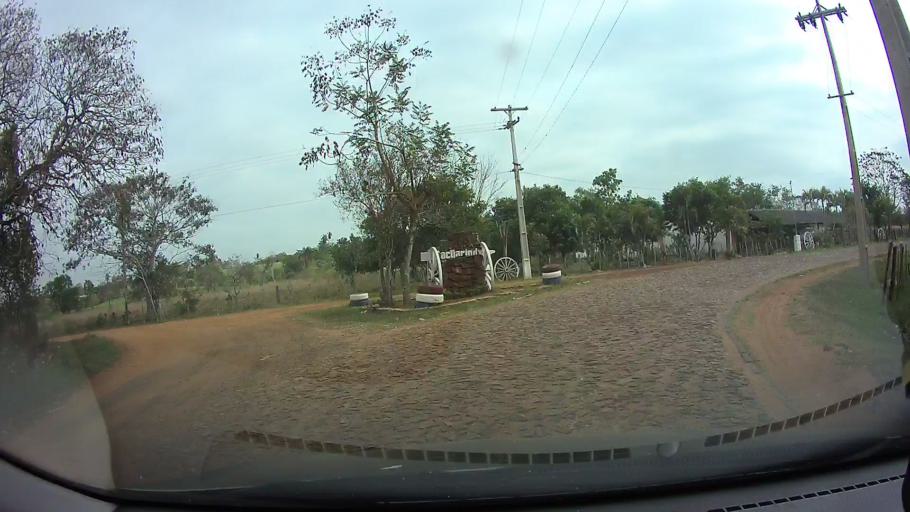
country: PY
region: Cordillera
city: Arroyos y Esteros
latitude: -25.0379
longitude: -57.1092
